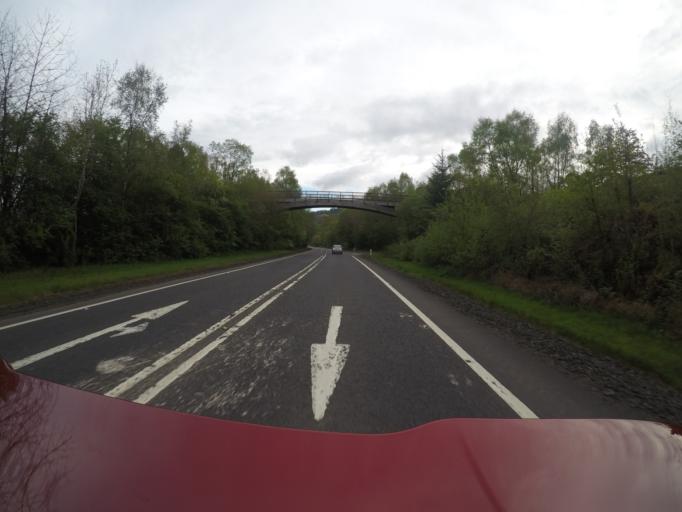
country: GB
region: Scotland
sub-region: West Dunbartonshire
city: Balloch
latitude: 56.1024
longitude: -4.6419
